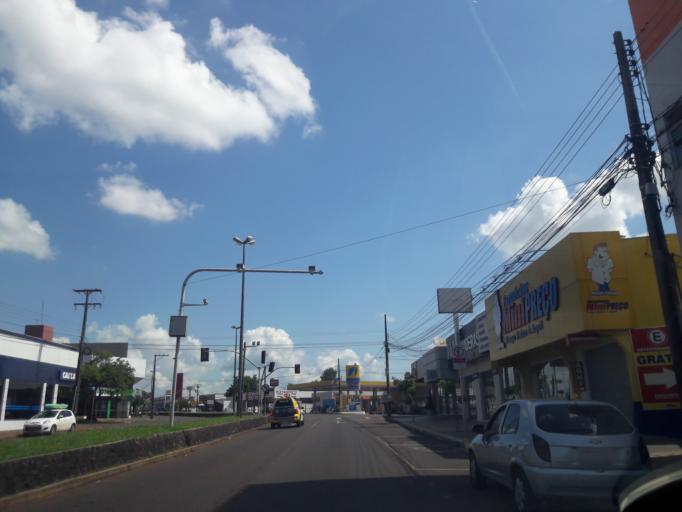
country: BR
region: Parana
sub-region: Cascavel
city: Cascavel
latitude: -24.9755
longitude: -53.4552
